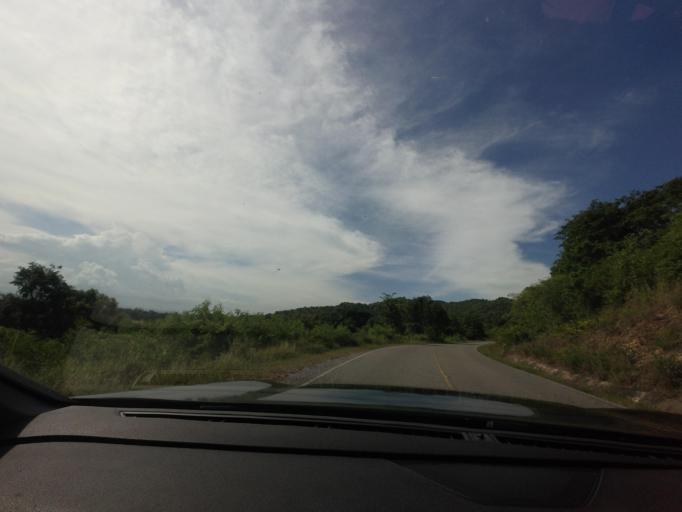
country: TH
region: Prachuap Khiri Khan
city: Hua Hin
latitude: 12.4959
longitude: 99.9467
